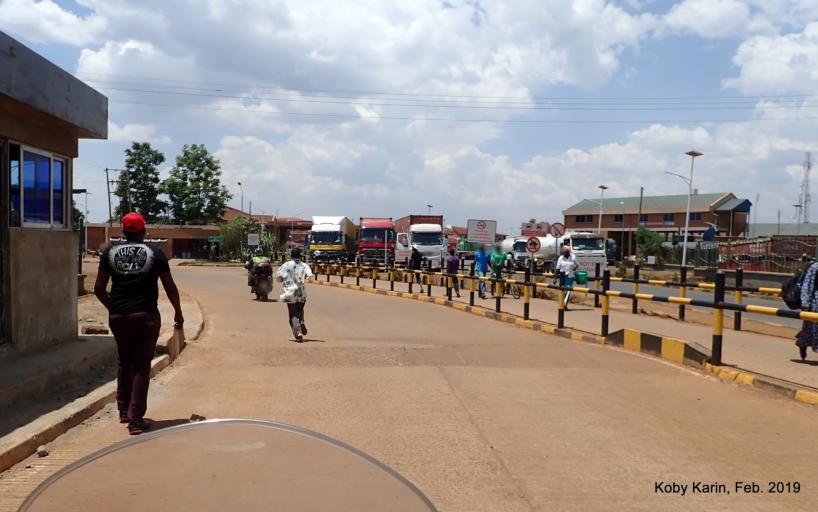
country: UG
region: Eastern Region
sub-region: Busia District
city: Busia
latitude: 0.4650
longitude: 34.1008
